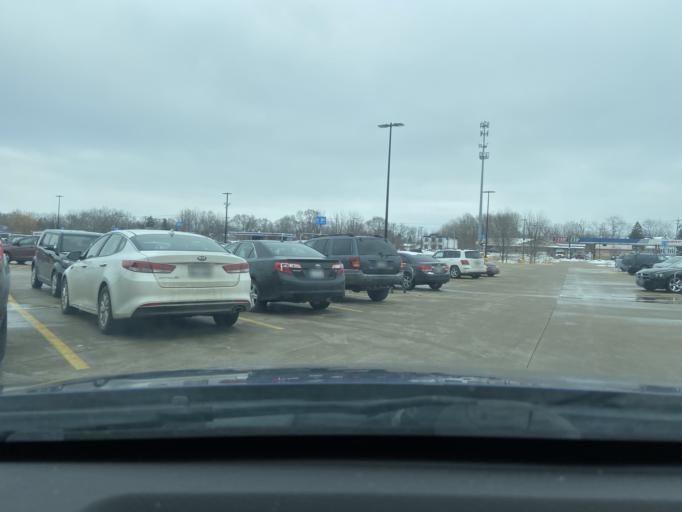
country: US
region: Illinois
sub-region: Lake County
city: Venetian Village
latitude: 42.3967
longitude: -88.0678
